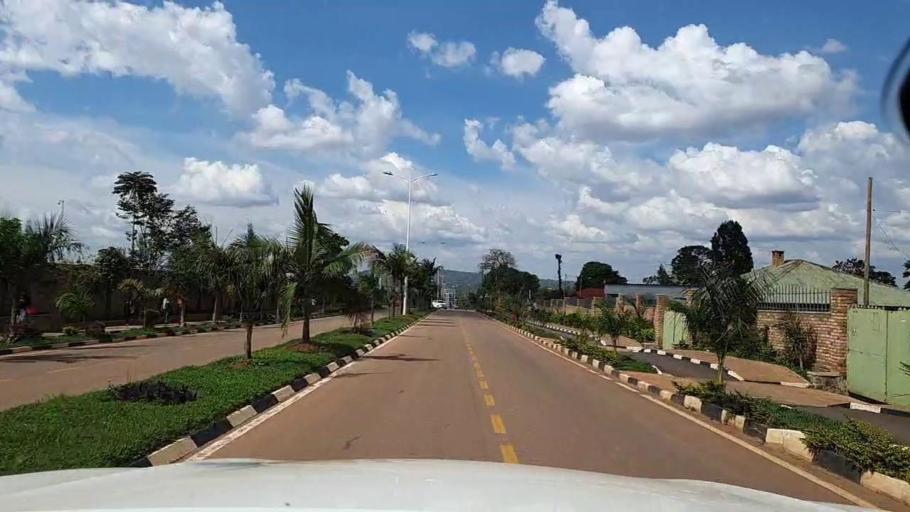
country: RW
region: Southern Province
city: Butare
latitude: -2.5966
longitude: 29.7427
